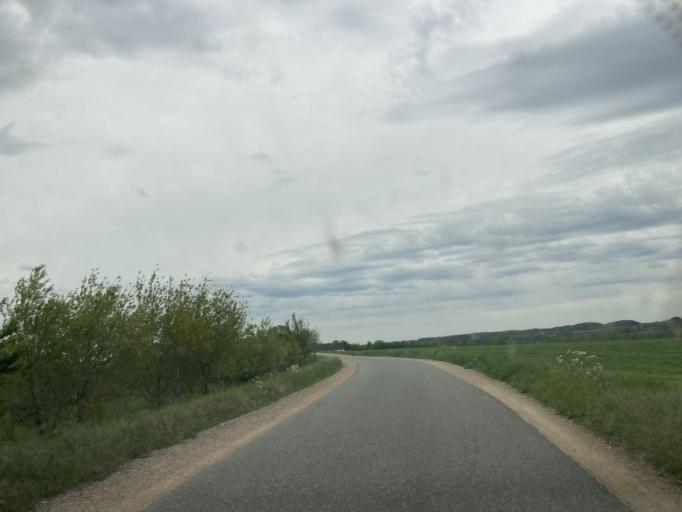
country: DK
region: Zealand
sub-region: Roskilde Kommune
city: Svogerslev
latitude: 55.6402
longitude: 11.9824
